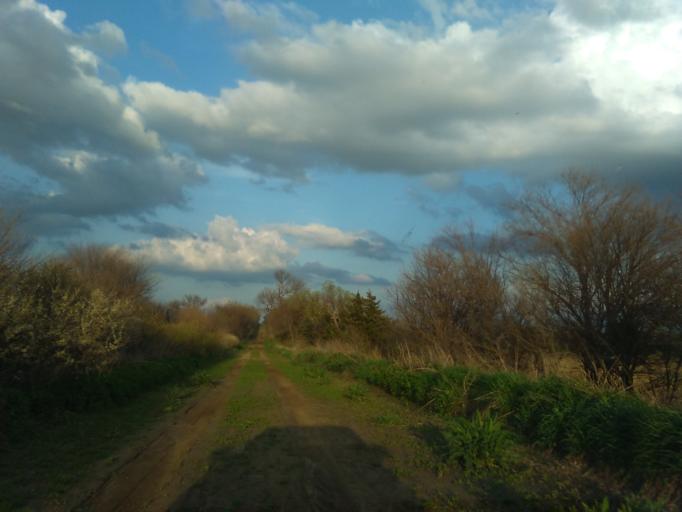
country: US
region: Nebraska
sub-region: Webster County
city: Red Cloud
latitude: 40.2055
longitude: -98.3890
